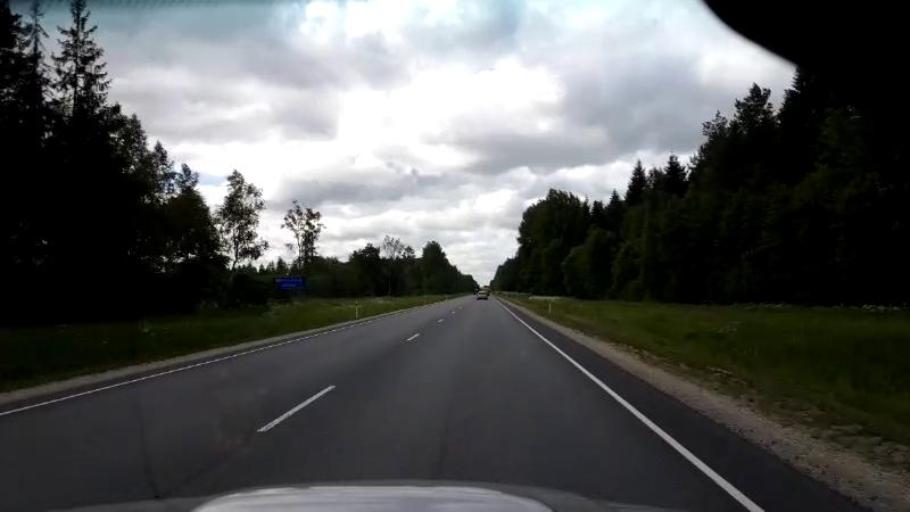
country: EE
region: Raplamaa
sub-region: Maerjamaa vald
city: Marjamaa
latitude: 58.7982
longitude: 24.4128
